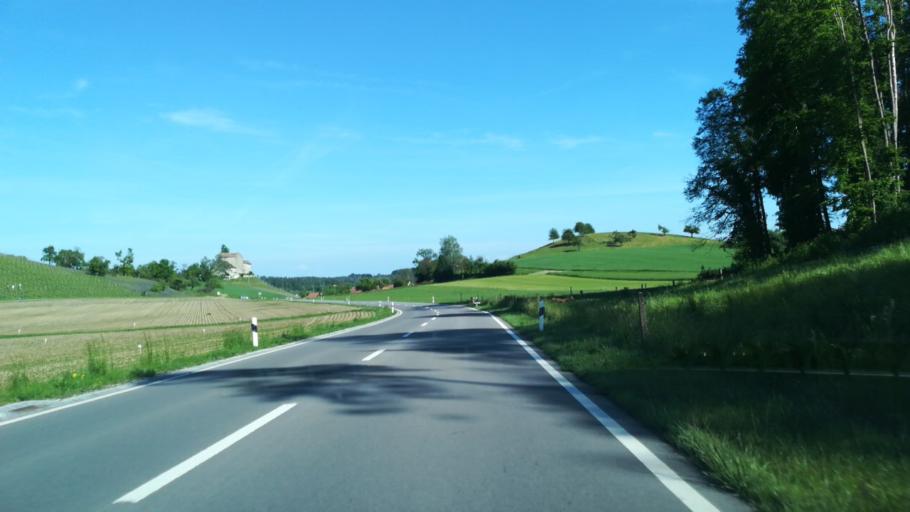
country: CH
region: Thurgau
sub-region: Frauenfeld District
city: Diessenhofen
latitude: 47.6253
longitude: 8.7695
